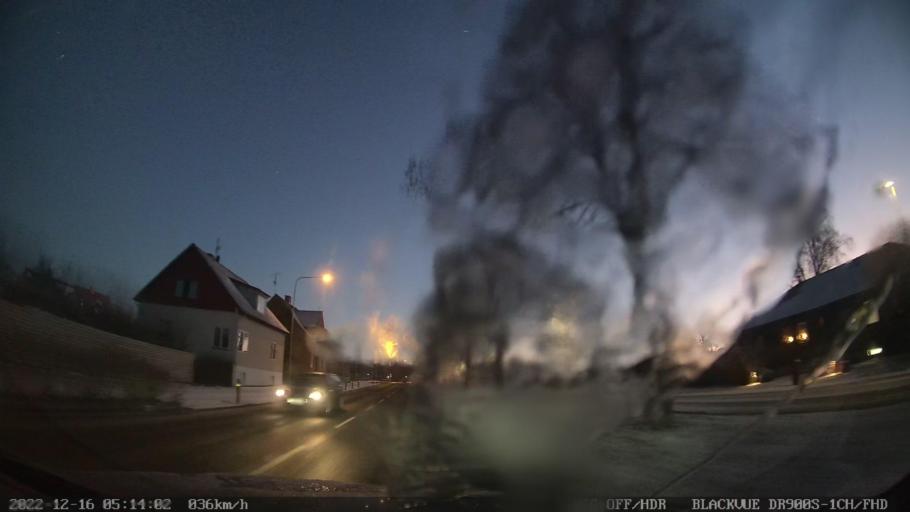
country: SE
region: Skane
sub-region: Tomelilla Kommun
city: Tomelilla
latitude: 55.5425
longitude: 13.9436
